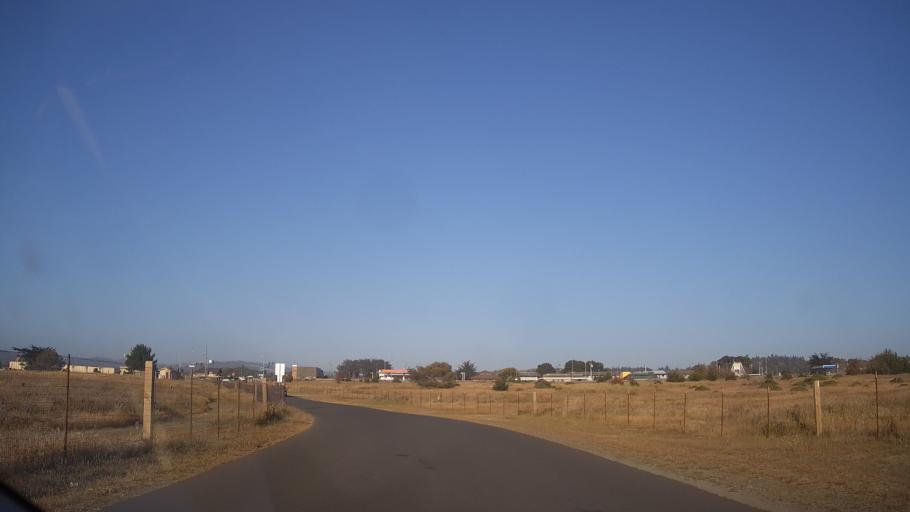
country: US
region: California
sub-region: Mendocino County
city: Fort Bragg
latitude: 39.4322
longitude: -123.8095
